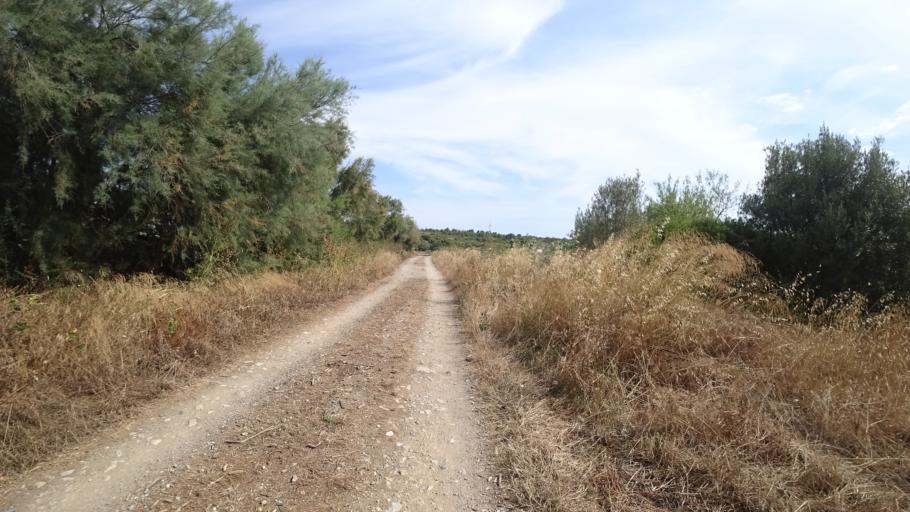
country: FR
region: Languedoc-Roussillon
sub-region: Departement de l'Aude
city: Leucate
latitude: 42.9037
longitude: 3.0385
